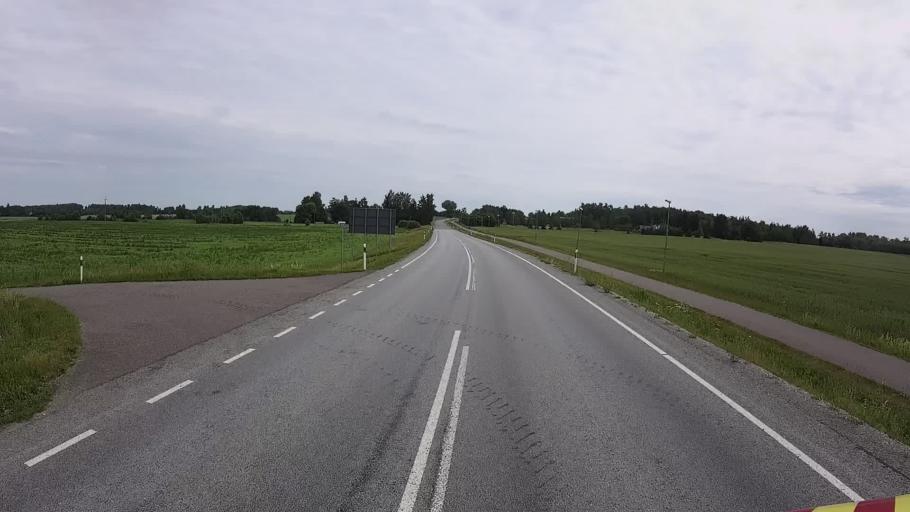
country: EE
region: Viljandimaa
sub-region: Karksi vald
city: Karksi-Nuia
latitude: 58.1113
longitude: 25.5697
